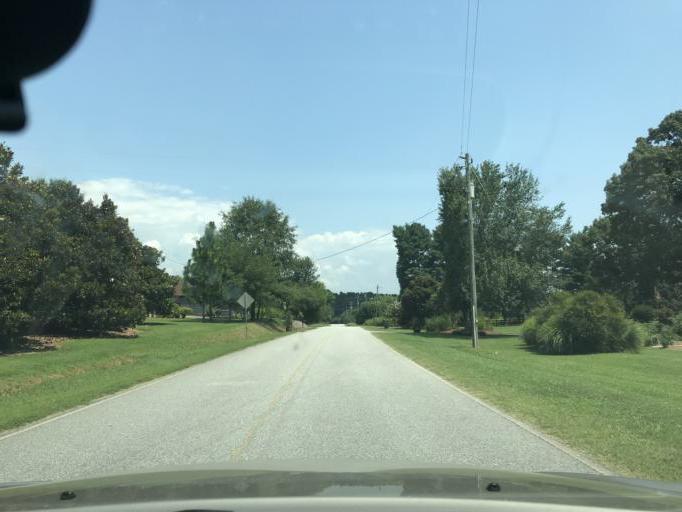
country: US
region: Georgia
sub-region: Dawson County
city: Dawsonville
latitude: 34.3357
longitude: -84.0763
